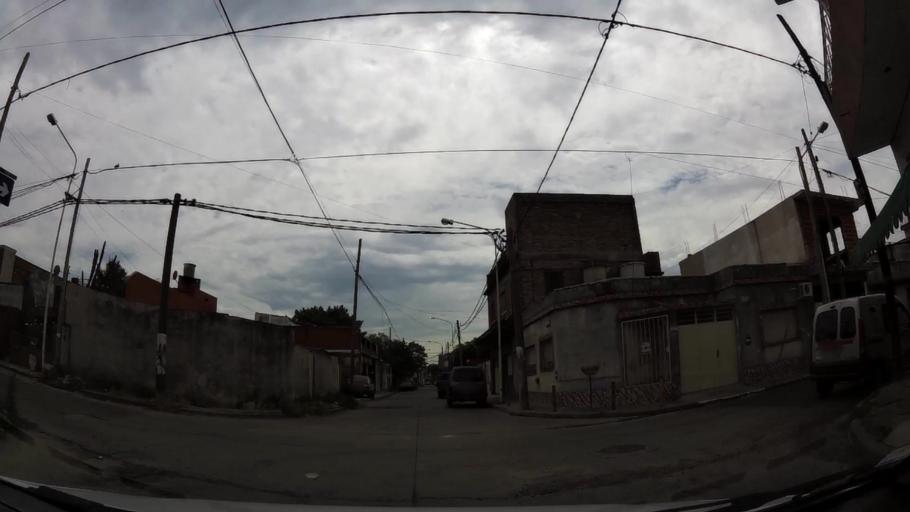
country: AR
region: Buenos Aires F.D.
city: Villa Lugano
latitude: -34.6852
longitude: -58.5111
